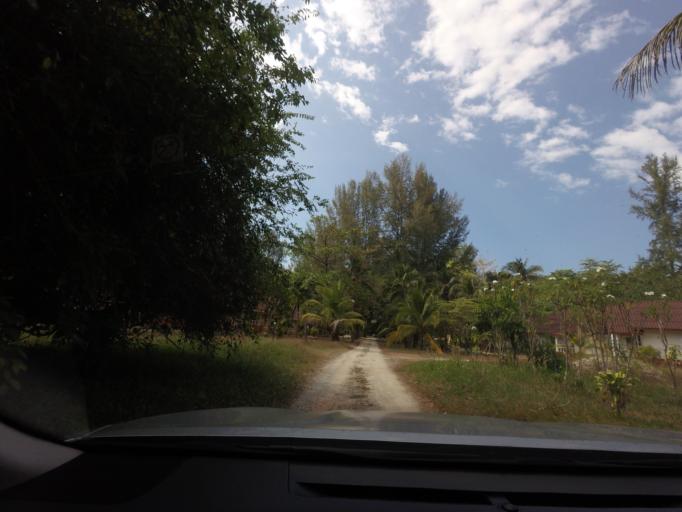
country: TH
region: Phangnga
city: Ban Khao Lak
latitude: 8.7374
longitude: 98.2435
